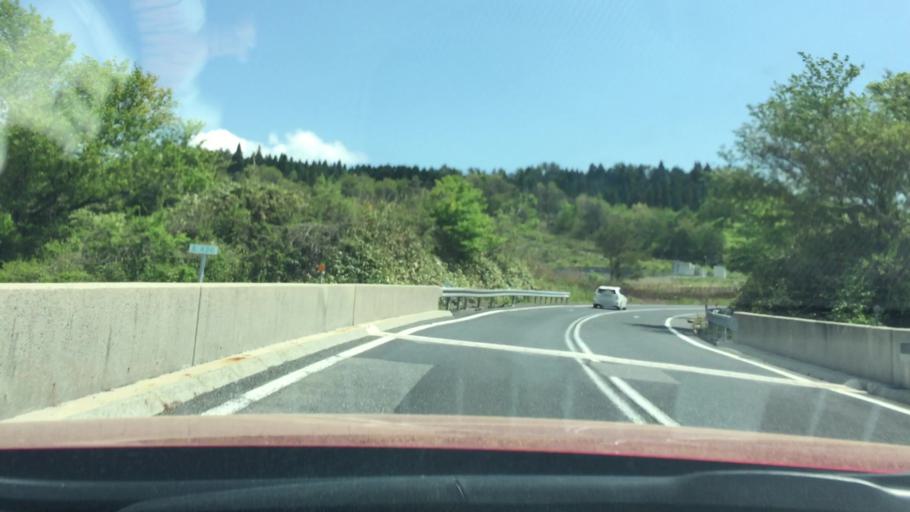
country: JP
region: Tottori
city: Kurayoshi
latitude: 35.2747
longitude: 133.6226
